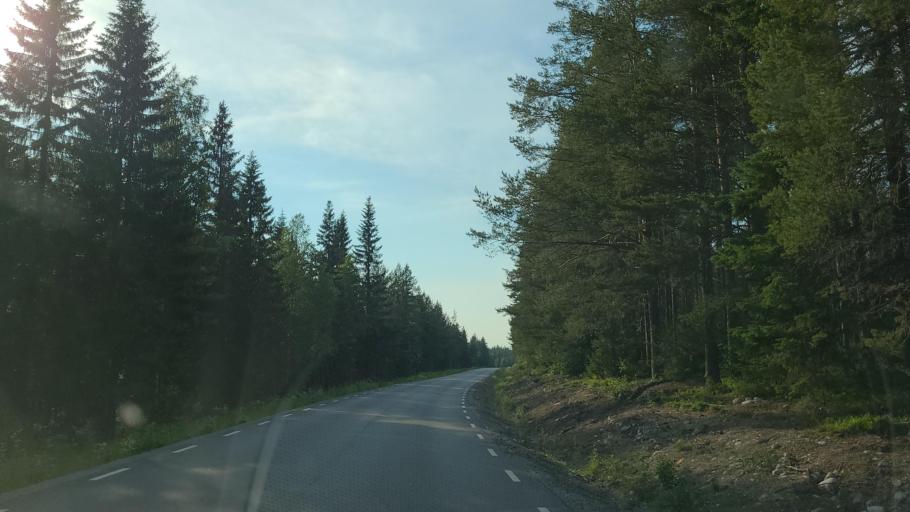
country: SE
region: Vaesterbotten
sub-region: Skelleftea Kommun
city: Burea
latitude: 64.4562
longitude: 21.4248
